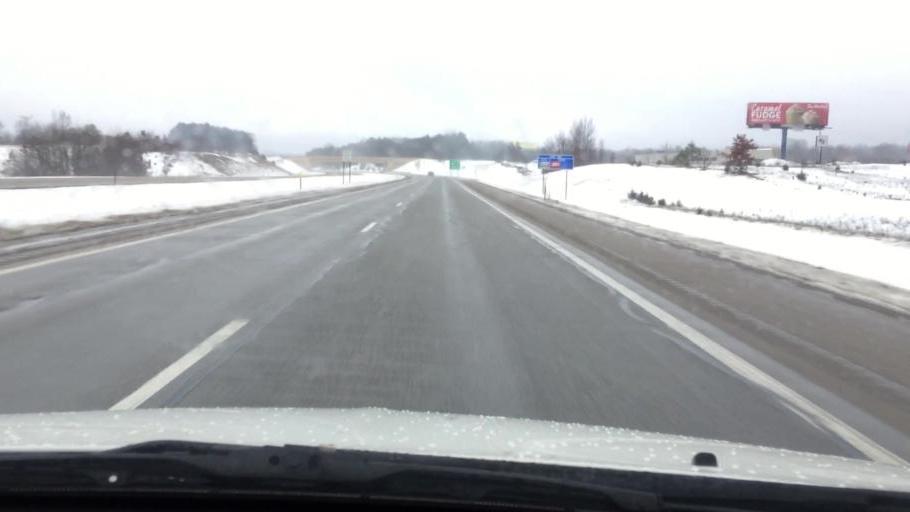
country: US
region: Michigan
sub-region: Wexford County
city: Cadillac
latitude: 44.2716
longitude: -85.3886
